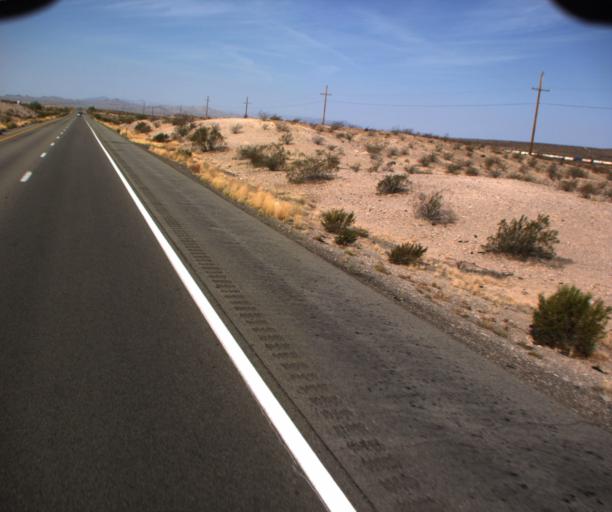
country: US
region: Arizona
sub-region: Mohave County
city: Desert Hills
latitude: 34.7736
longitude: -114.1908
